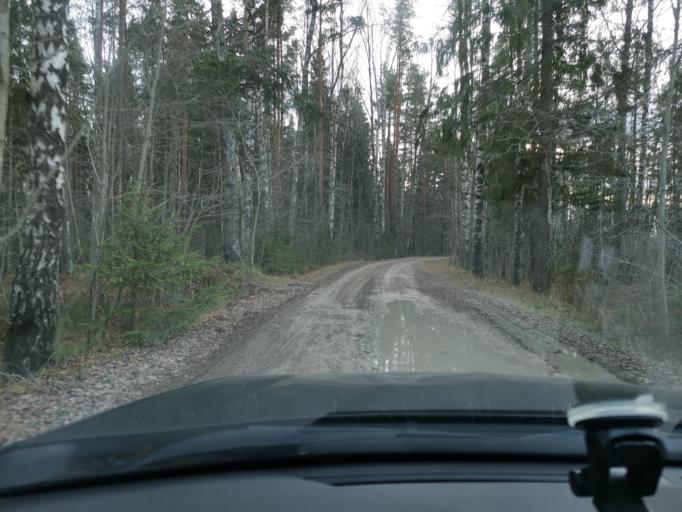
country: EE
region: Ida-Virumaa
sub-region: Sillamaee linn
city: Sillamae
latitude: 59.2574
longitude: 27.9145
